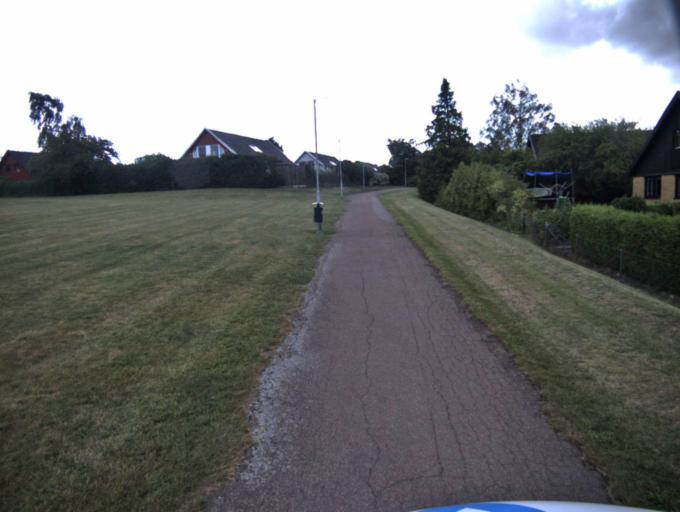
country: SE
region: Skane
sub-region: Kavlinge Kommun
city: Kaevlinge
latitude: 55.7794
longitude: 13.1114
